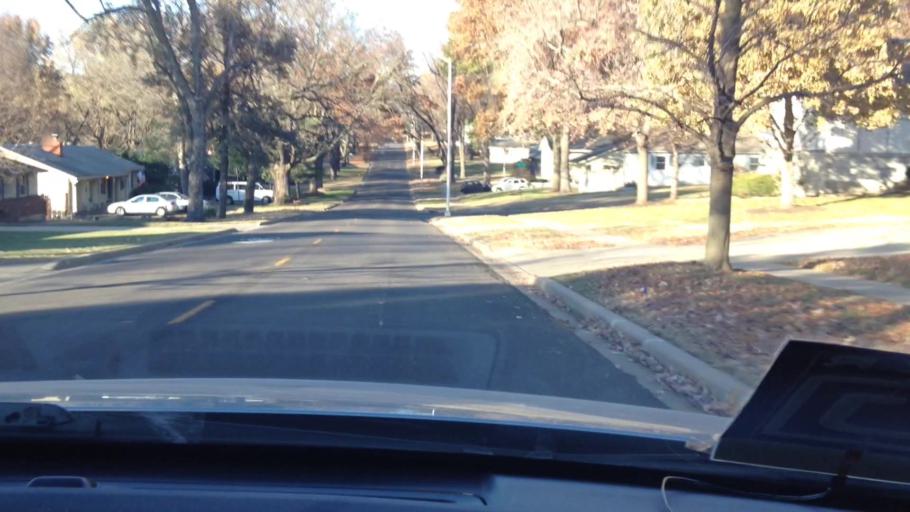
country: US
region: Kansas
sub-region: Johnson County
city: Overland Park
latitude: 38.9725
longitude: -94.6583
